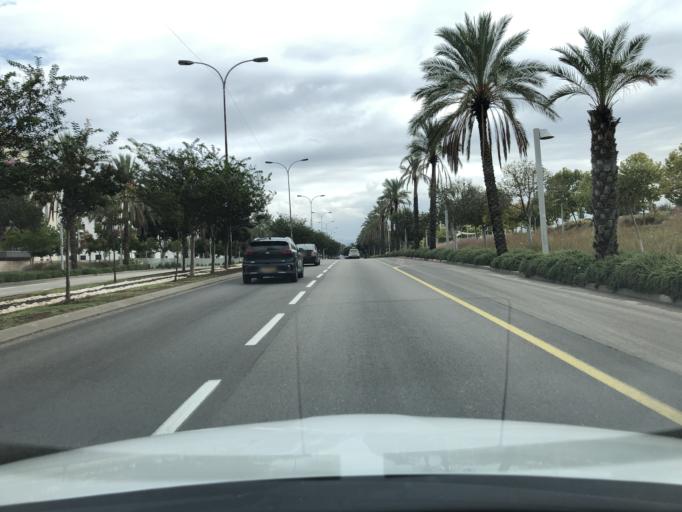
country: IL
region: Central District
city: Modiin
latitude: 31.9096
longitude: 35.0102
